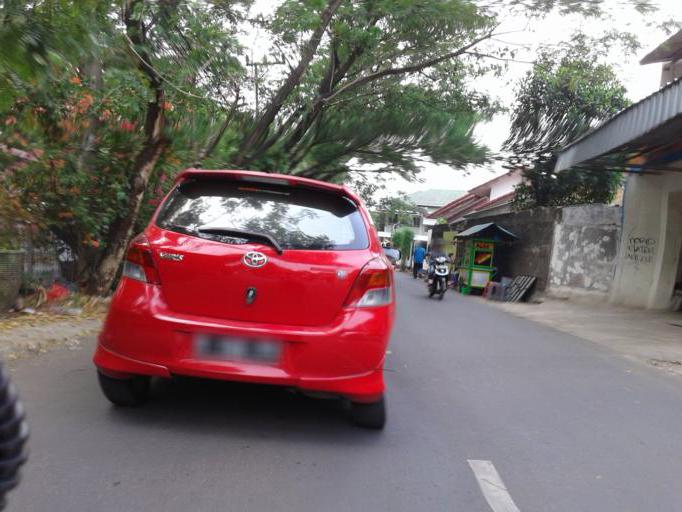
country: ID
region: West Java
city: Pamulang
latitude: -6.3232
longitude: 106.7639
